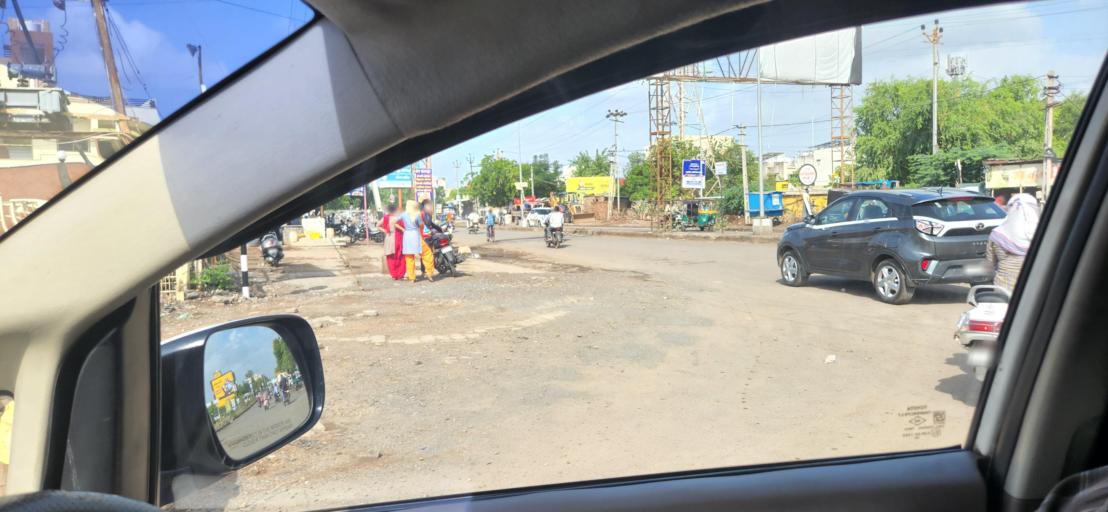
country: IN
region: Gujarat
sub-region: Bhavnagar
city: Bhavnagar
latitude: 21.7380
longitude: 72.1477
